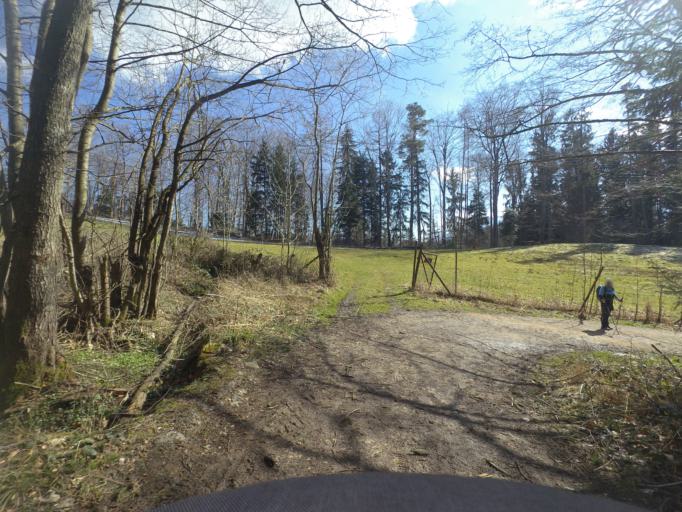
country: DE
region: Bavaria
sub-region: Upper Bavaria
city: Piding
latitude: 47.7947
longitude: 12.9174
